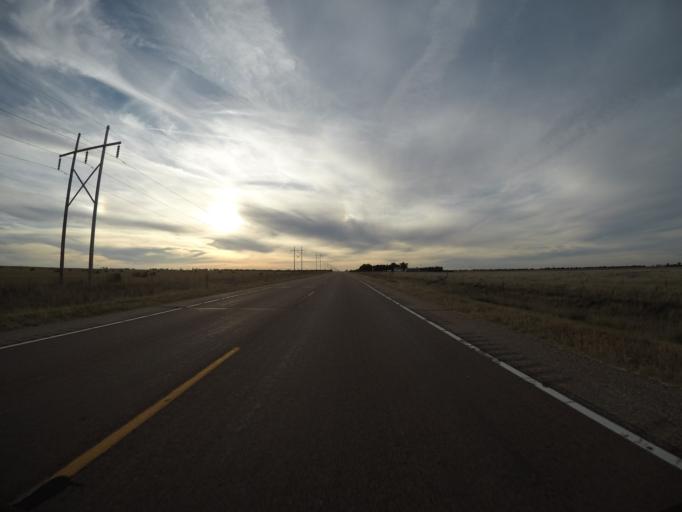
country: US
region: Colorado
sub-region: Yuma County
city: Yuma
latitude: 39.6557
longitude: -102.7417
